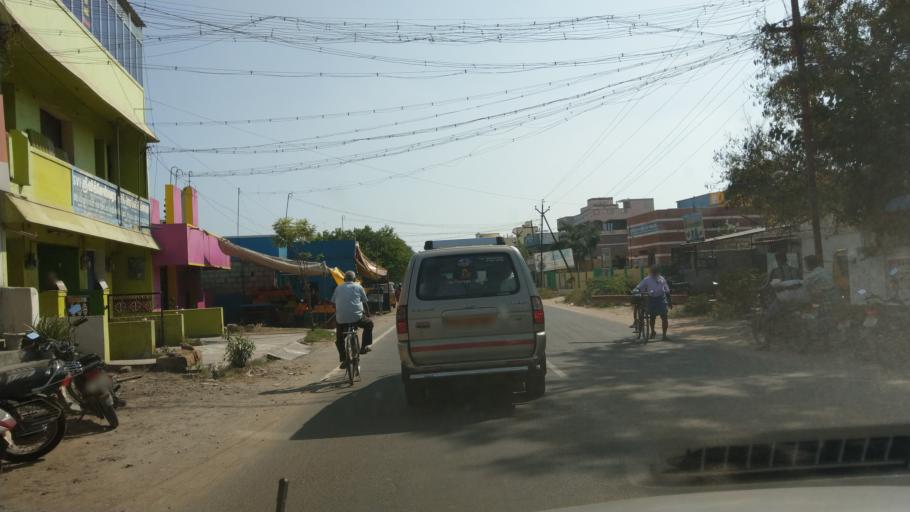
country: IN
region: Tamil Nadu
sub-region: Vellore
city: Arcot
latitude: 12.8960
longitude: 79.3196
